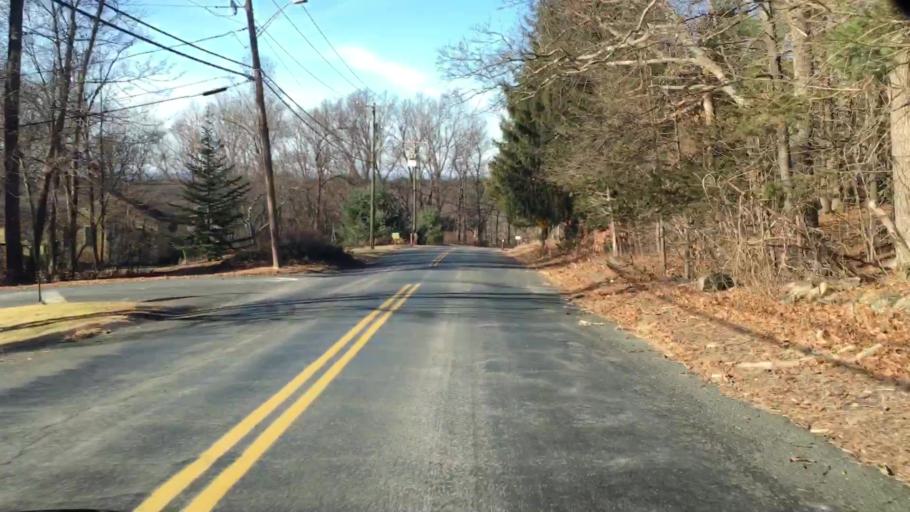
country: US
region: Connecticut
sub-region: Tolland County
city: Somers
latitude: 41.9712
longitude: -72.4410
